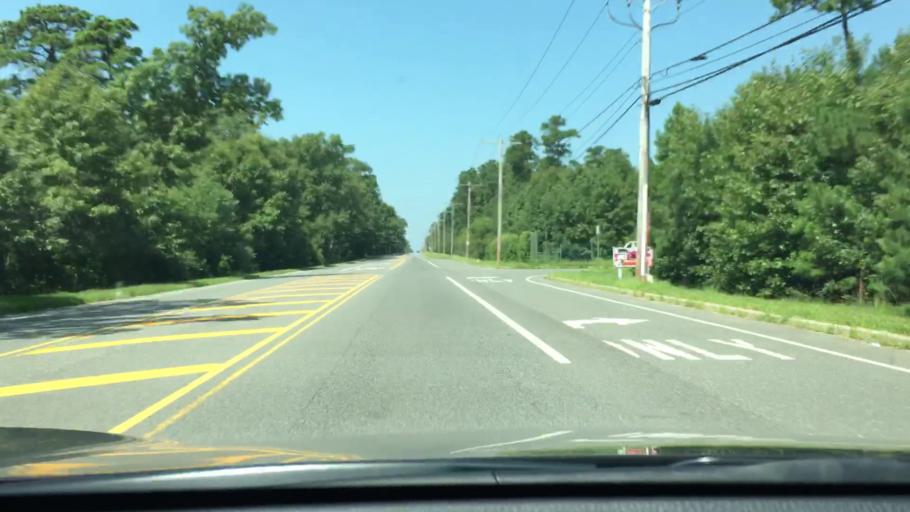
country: US
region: New Jersey
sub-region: Cumberland County
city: Laurel Lake
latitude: 39.3552
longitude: -75.0638
